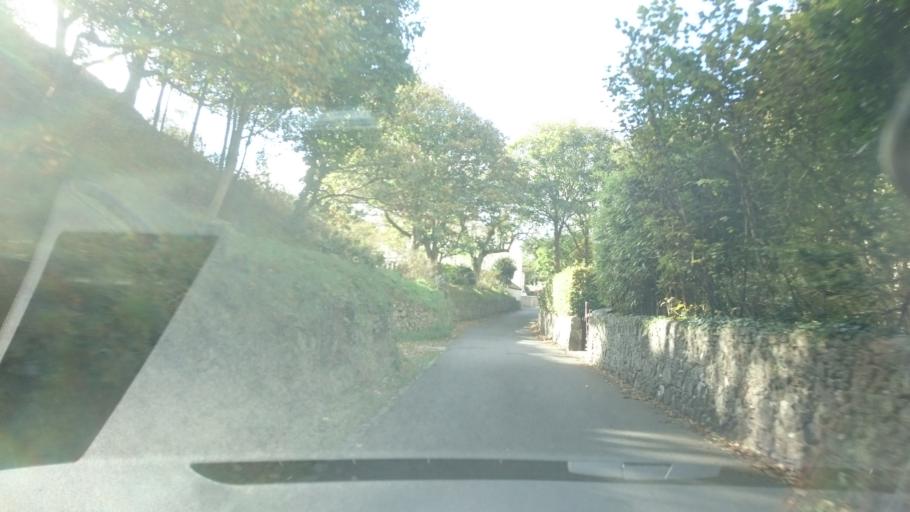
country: GG
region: St Peter Port
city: Saint Peter Port
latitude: 49.4306
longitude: -2.6638
